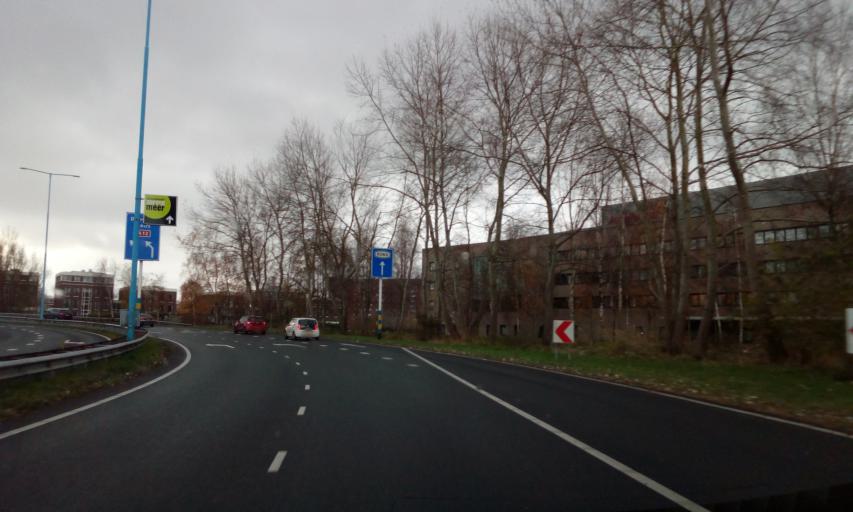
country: NL
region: South Holland
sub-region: Gemeente Zoetermeer
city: Zoetermeer
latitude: 52.0469
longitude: 4.4718
